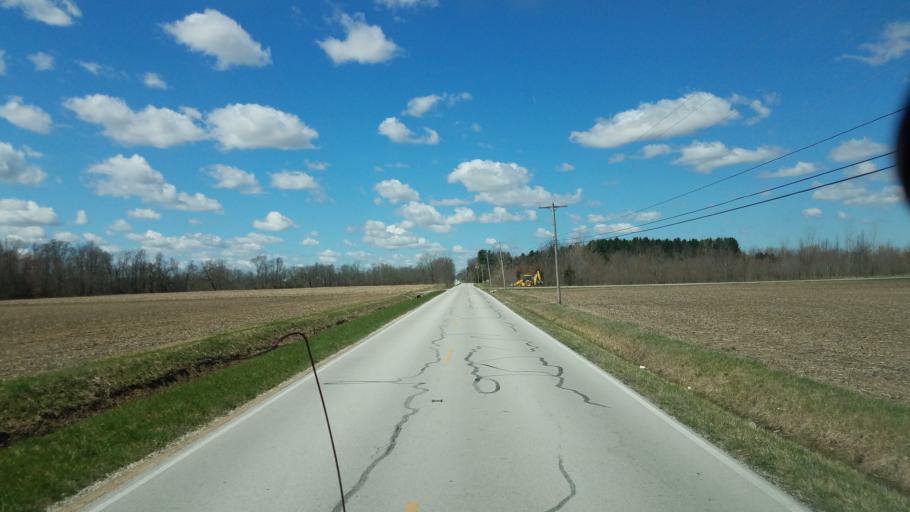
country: US
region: Ohio
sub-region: Sandusky County
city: Green Springs
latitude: 41.2569
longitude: -83.0707
